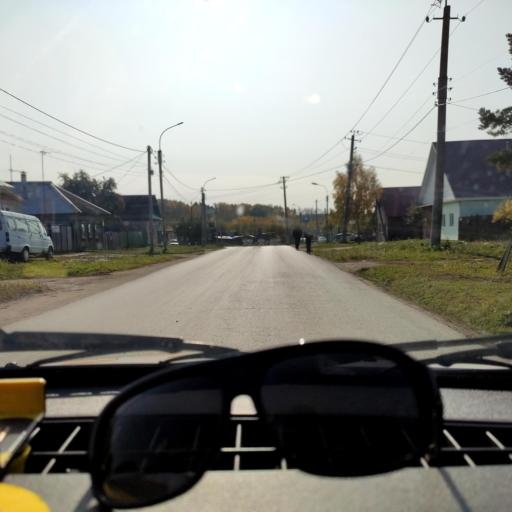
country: RU
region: Bashkortostan
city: Blagoveshchensk
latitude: 55.0254
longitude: 55.9895
